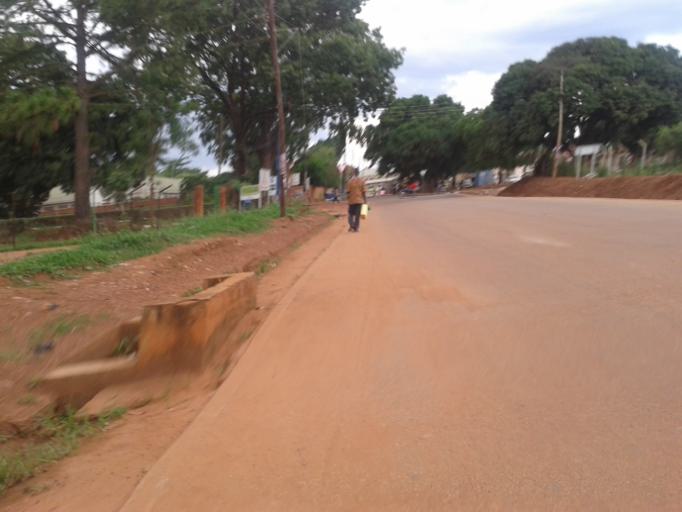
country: UG
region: Northern Region
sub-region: Gulu District
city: Gulu
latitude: 2.7773
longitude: 32.2966
